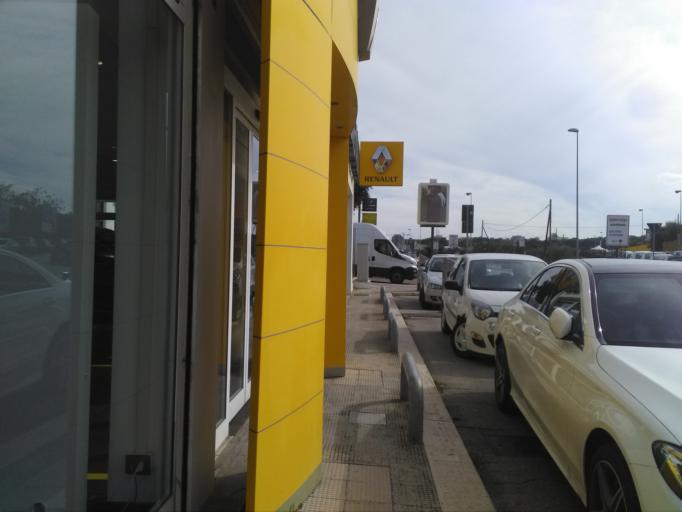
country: IT
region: Apulia
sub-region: Provincia di Bari
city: Bari
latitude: 41.1131
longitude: 16.8987
